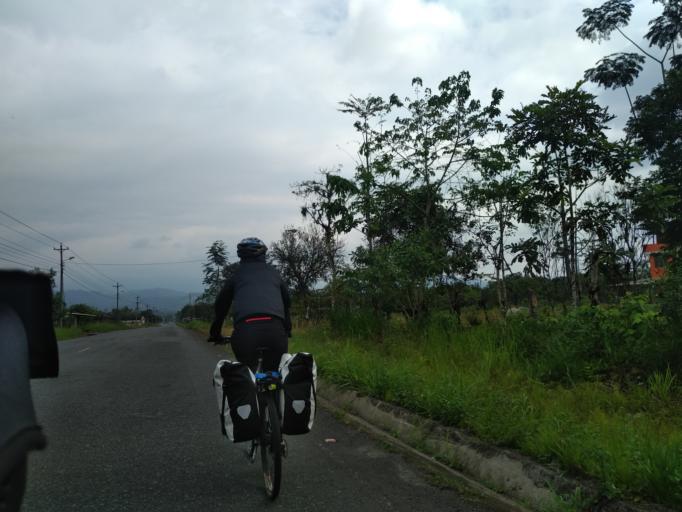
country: EC
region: Cotopaxi
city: La Mana
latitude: -0.8927
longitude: -79.1616
